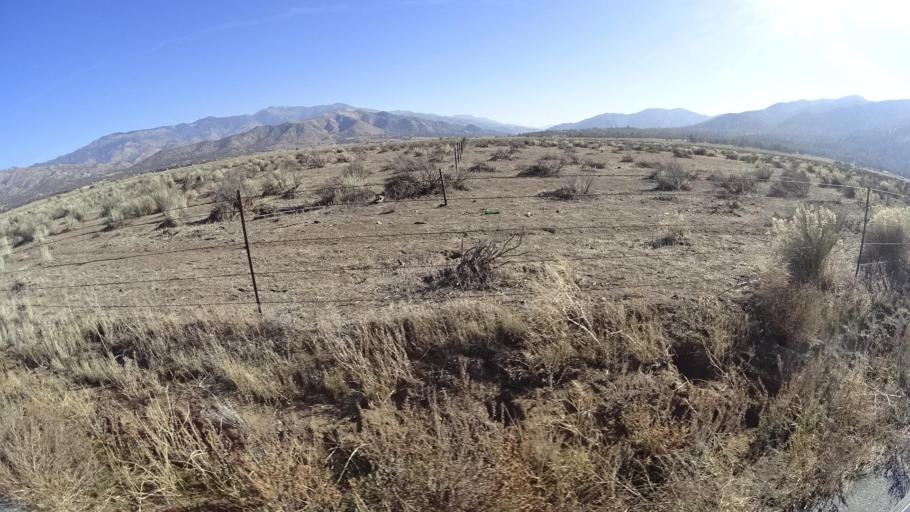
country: US
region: California
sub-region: Kern County
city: Bodfish
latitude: 35.4065
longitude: -118.5234
